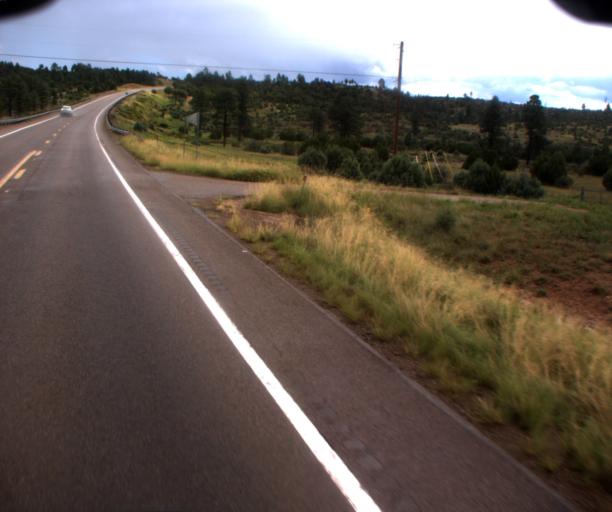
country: US
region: Arizona
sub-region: Navajo County
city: Heber-Overgaard
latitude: 34.3680
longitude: -110.4065
